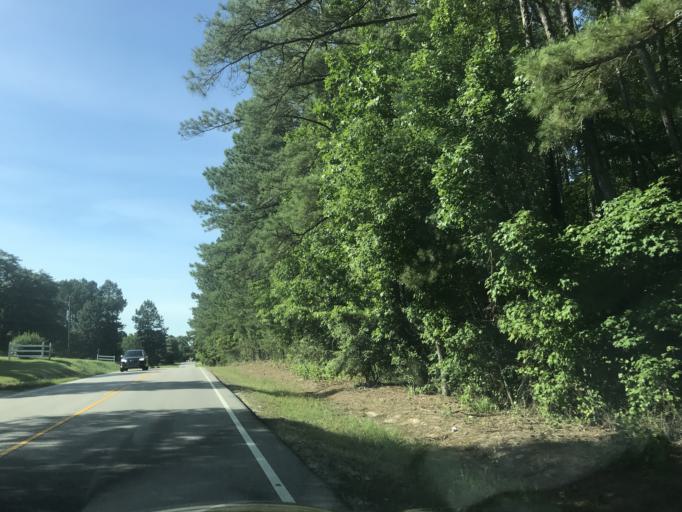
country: US
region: North Carolina
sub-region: Wake County
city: Garner
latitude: 35.6741
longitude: -78.5765
